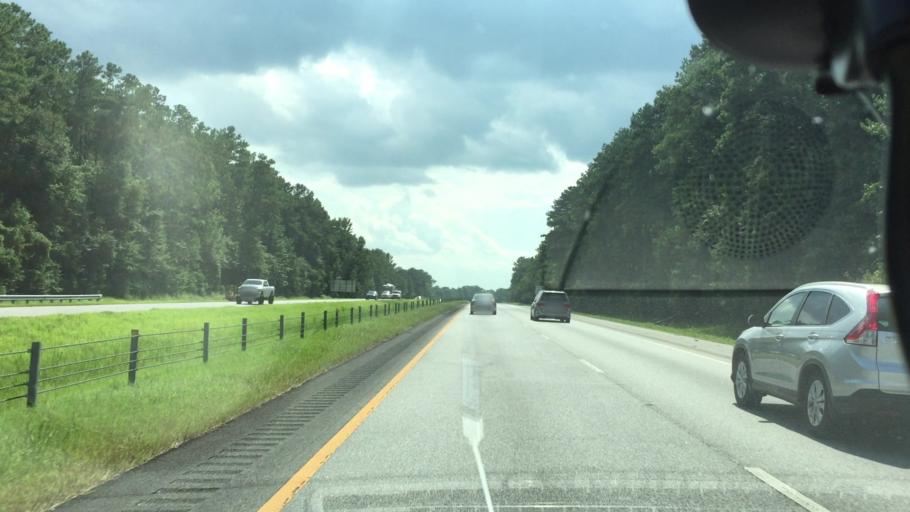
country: US
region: Alabama
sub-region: Macon County
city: Tuskegee
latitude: 32.4818
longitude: -85.6483
